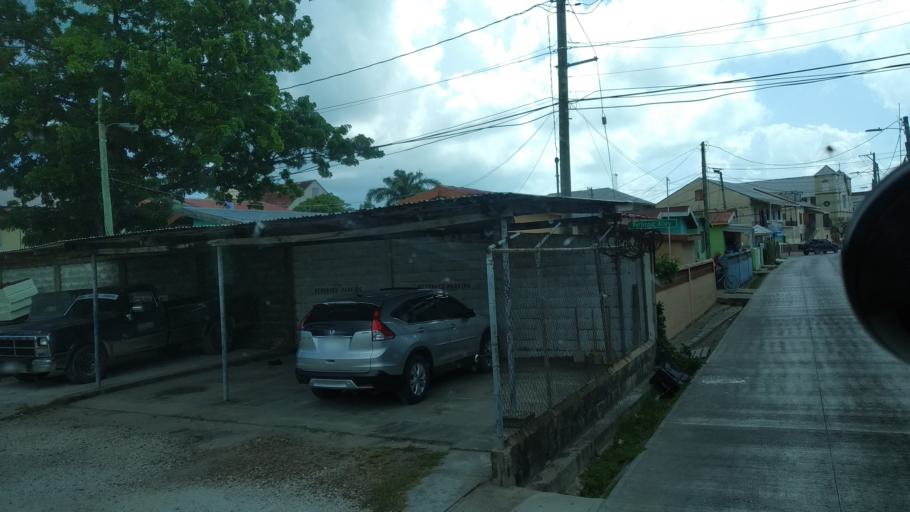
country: BZ
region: Belize
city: Belize City
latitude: 17.4972
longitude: -88.1884
